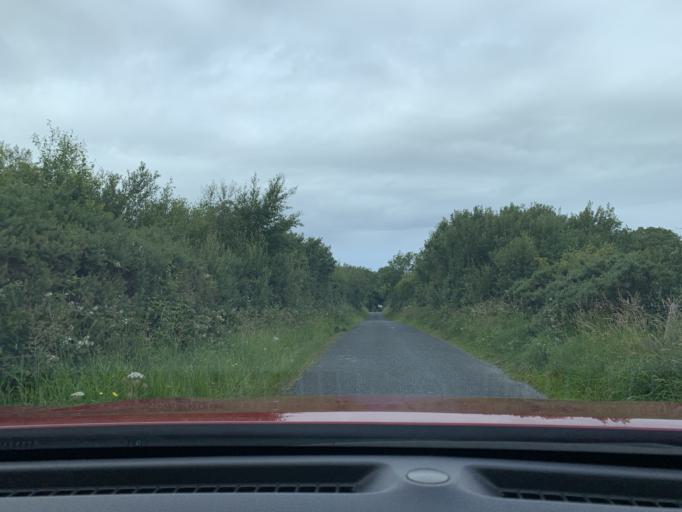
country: IE
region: Connaught
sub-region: County Leitrim
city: Kinlough
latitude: 54.3988
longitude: -8.4025
